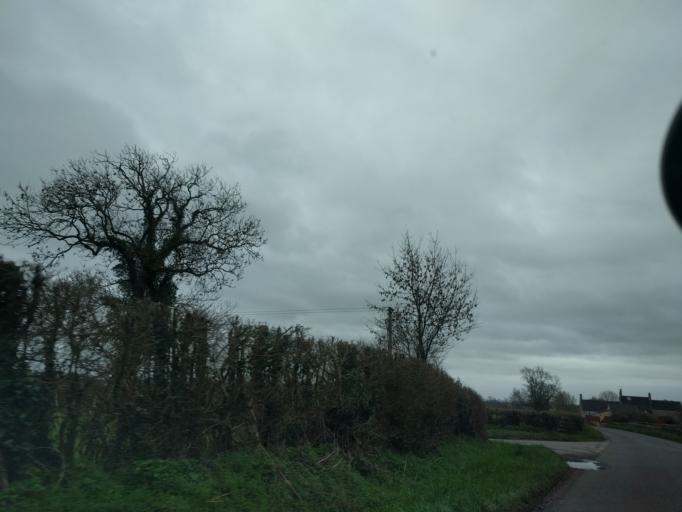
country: GB
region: England
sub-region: Wiltshire
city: Biddestone
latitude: 51.4974
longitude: -2.1947
